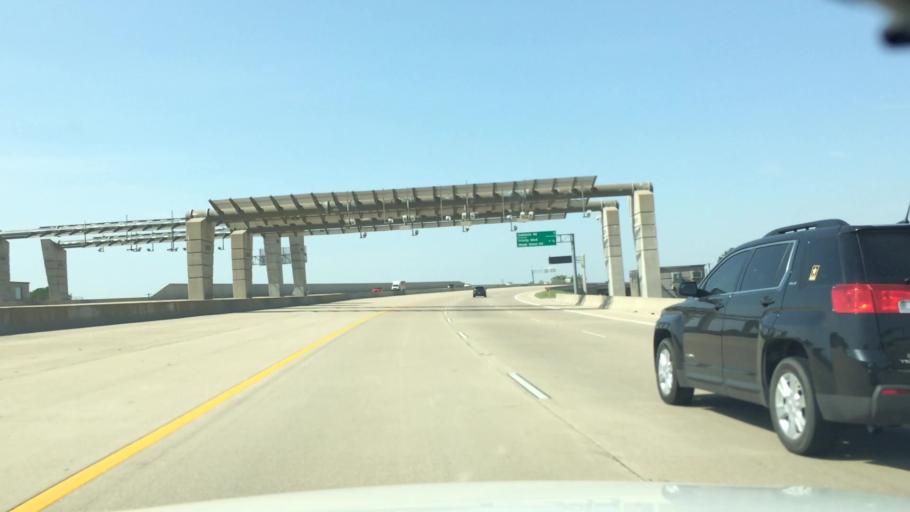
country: US
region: Texas
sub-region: Dallas County
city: Grand Prairie
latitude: 32.7753
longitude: -97.0272
